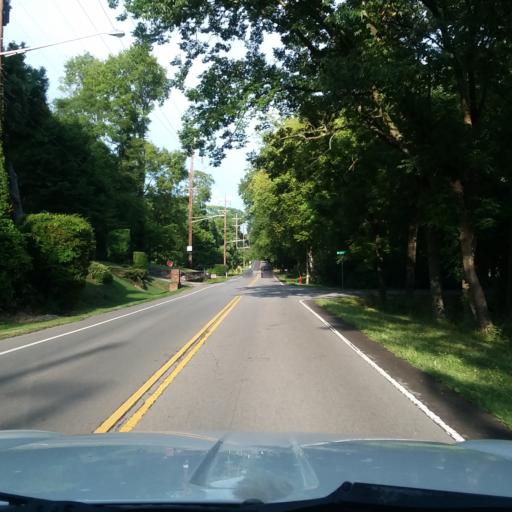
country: US
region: Tennessee
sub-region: Davidson County
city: Oak Hill
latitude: 36.0657
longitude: -86.7661
